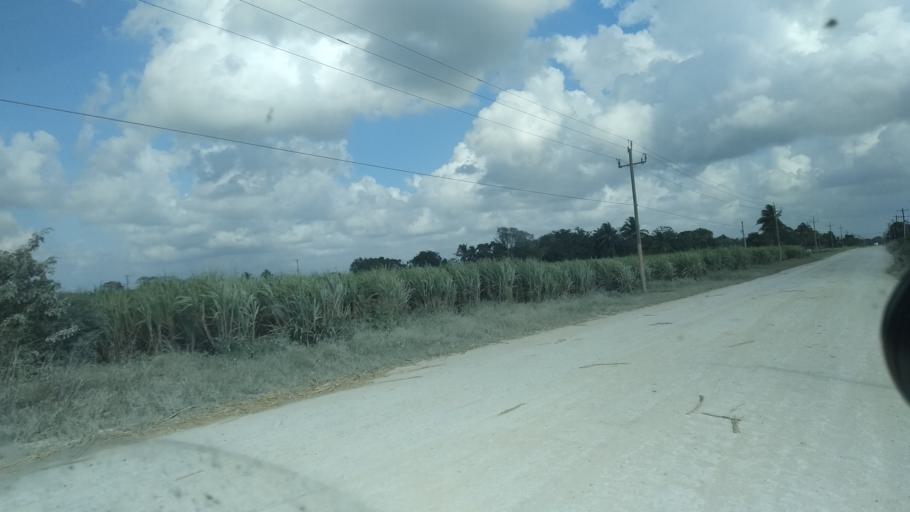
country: BZ
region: Corozal
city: Corozal
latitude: 18.3430
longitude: -88.4968
